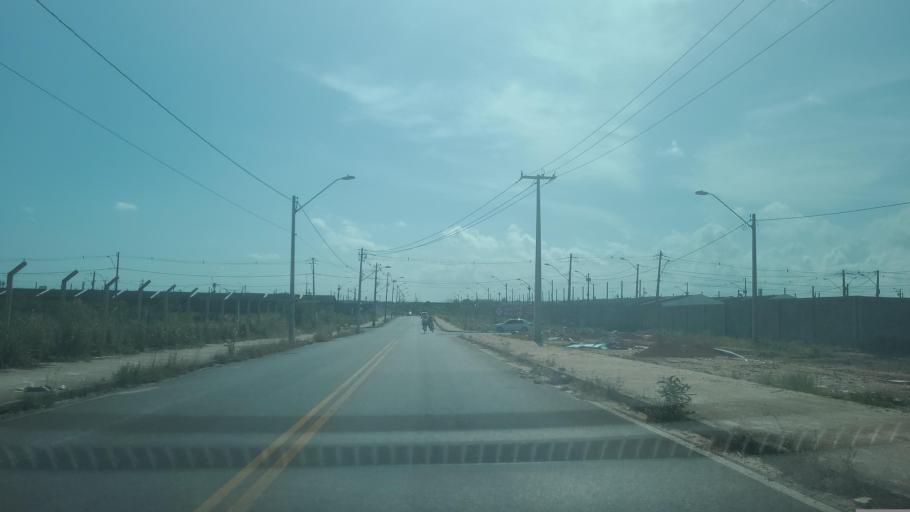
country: BR
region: Alagoas
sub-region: Satuba
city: Satuba
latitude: -9.5250
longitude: -35.7745
